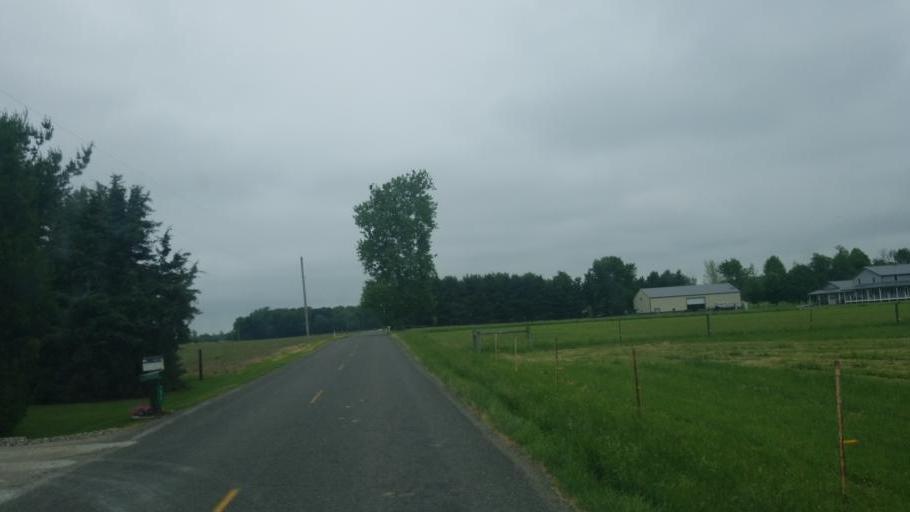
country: US
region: Indiana
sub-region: Elkhart County
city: Nappanee
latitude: 41.4678
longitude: -86.0497
